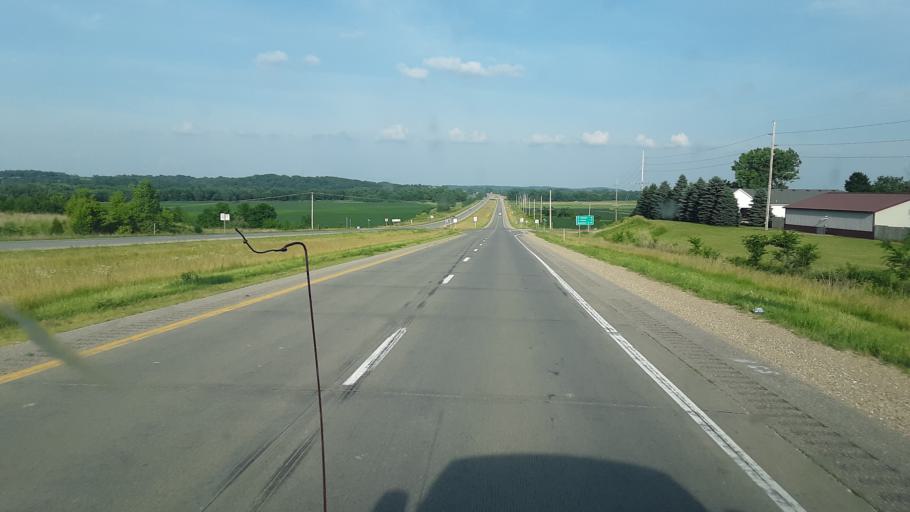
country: US
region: Iowa
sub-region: Tama County
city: Toledo
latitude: 42.0054
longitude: -92.7325
